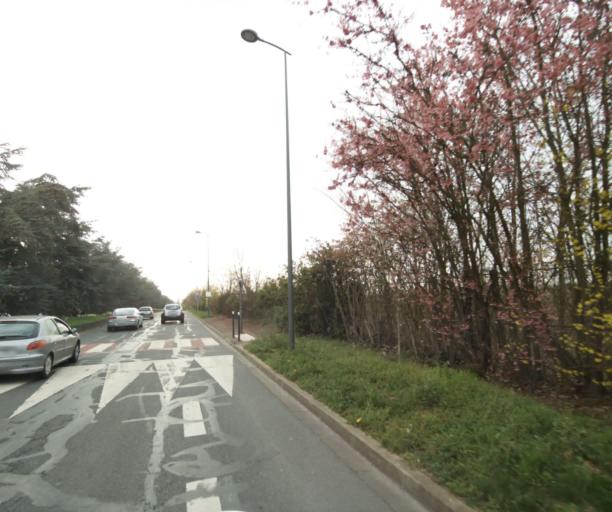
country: FR
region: Ile-de-France
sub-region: Departement du Val-d'Oise
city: Osny
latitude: 49.0473
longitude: 2.0555
